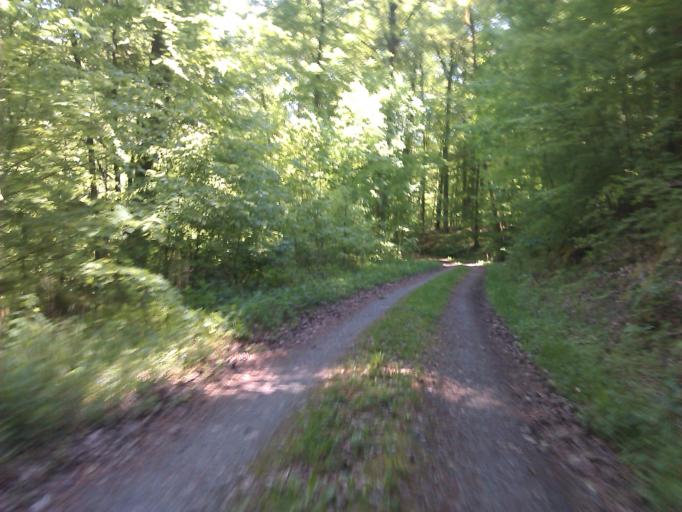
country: DE
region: Baden-Wuerttemberg
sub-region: Regierungsbezirk Stuttgart
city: Zaberfeld
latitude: 49.0451
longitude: 8.9003
